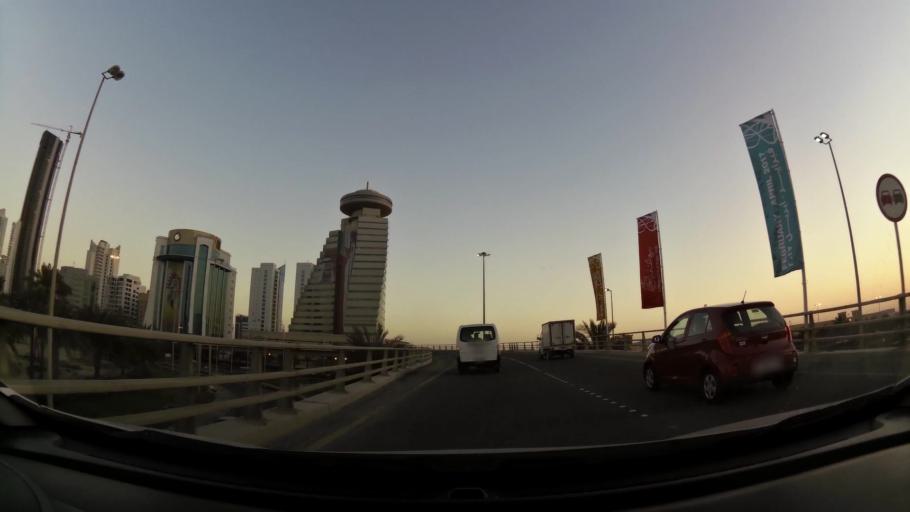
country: BH
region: Manama
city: Jidd Hafs
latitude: 26.2327
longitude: 50.5438
